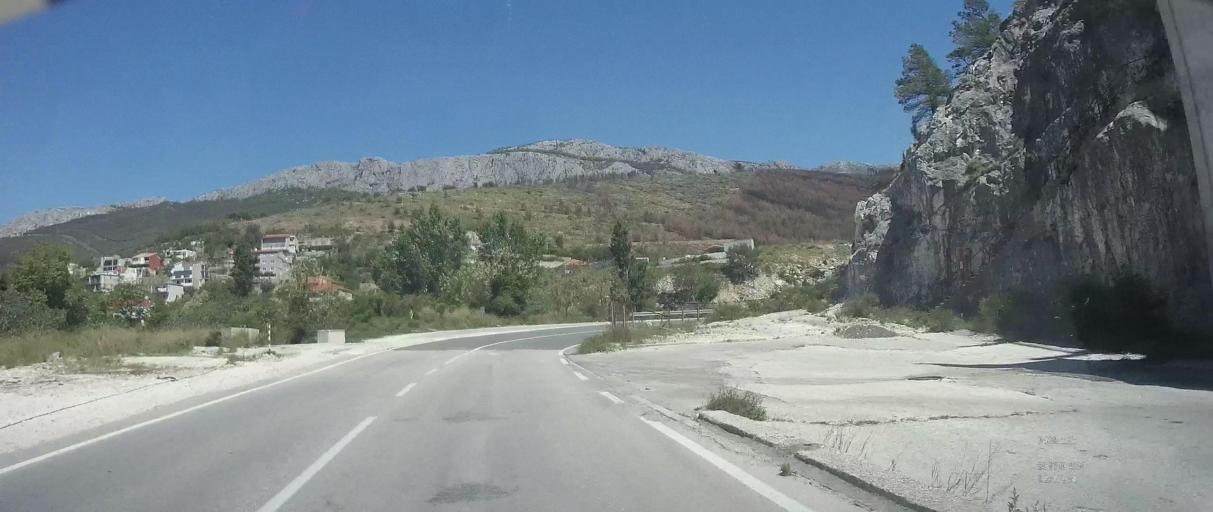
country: HR
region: Splitsko-Dalmatinska
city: Zrnovnica
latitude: 43.5180
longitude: 16.5437
